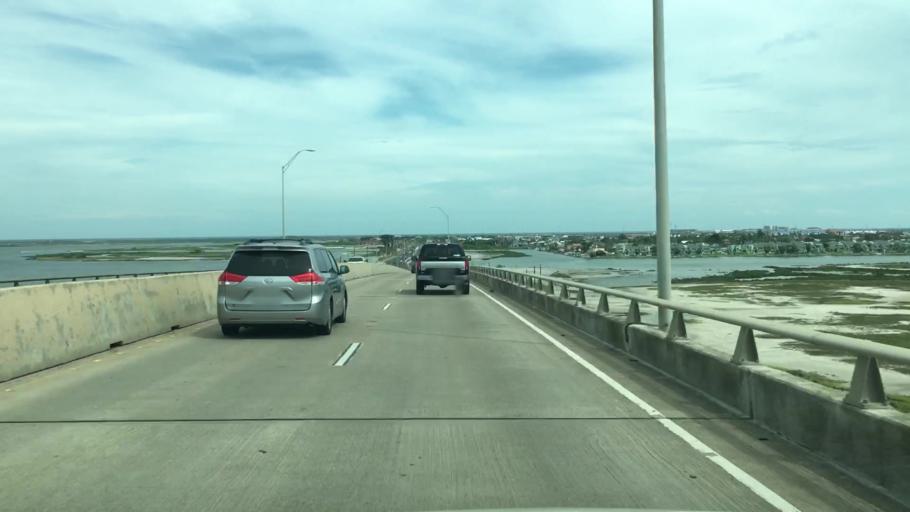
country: US
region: Texas
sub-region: Nueces County
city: Corpus Christi
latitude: 27.6343
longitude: -97.2389
